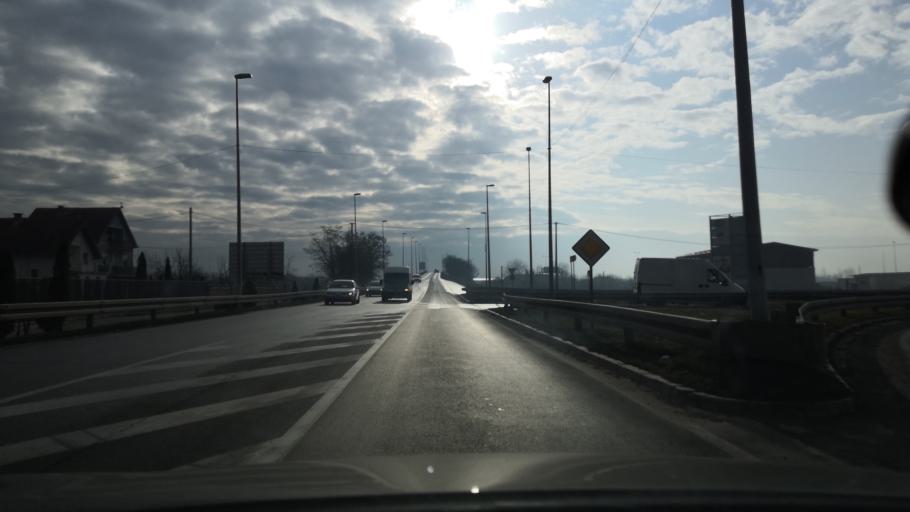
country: RS
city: Dobanovci
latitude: 44.8473
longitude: 20.2095
